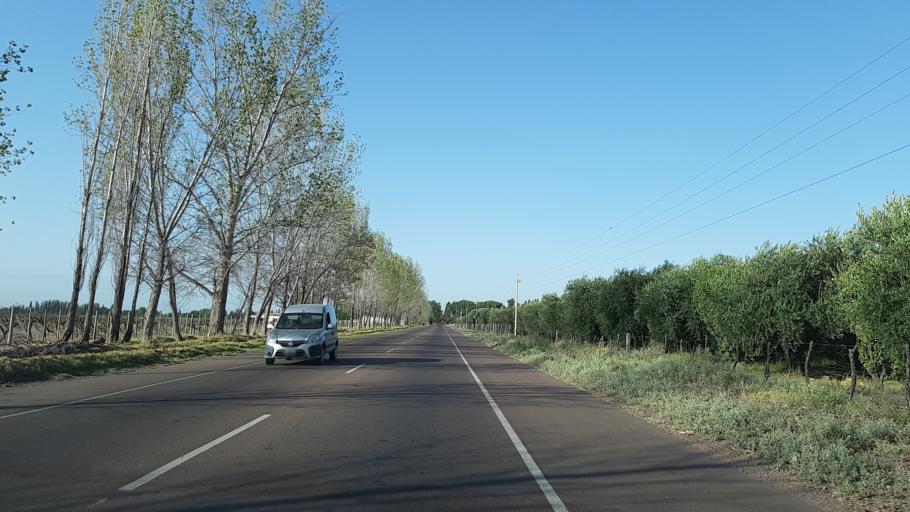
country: AR
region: Mendoza
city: San Martin
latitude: -32.9524
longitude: -68.4307
